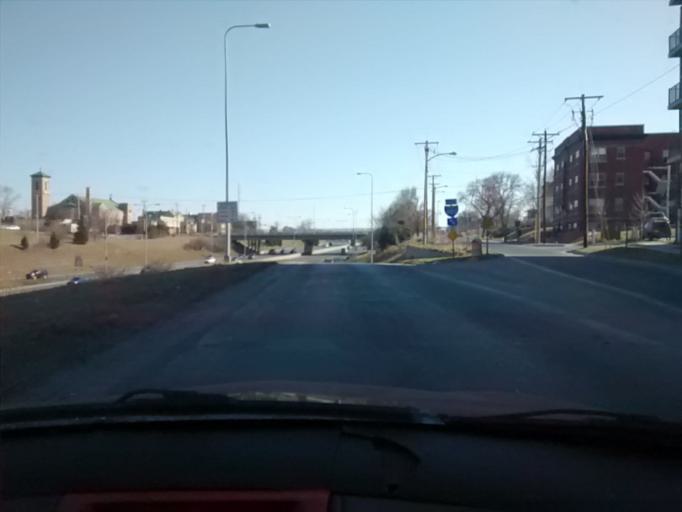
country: US
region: Nebraska
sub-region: Douglas County
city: Omaha
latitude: 41.2559
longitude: -95.9545
